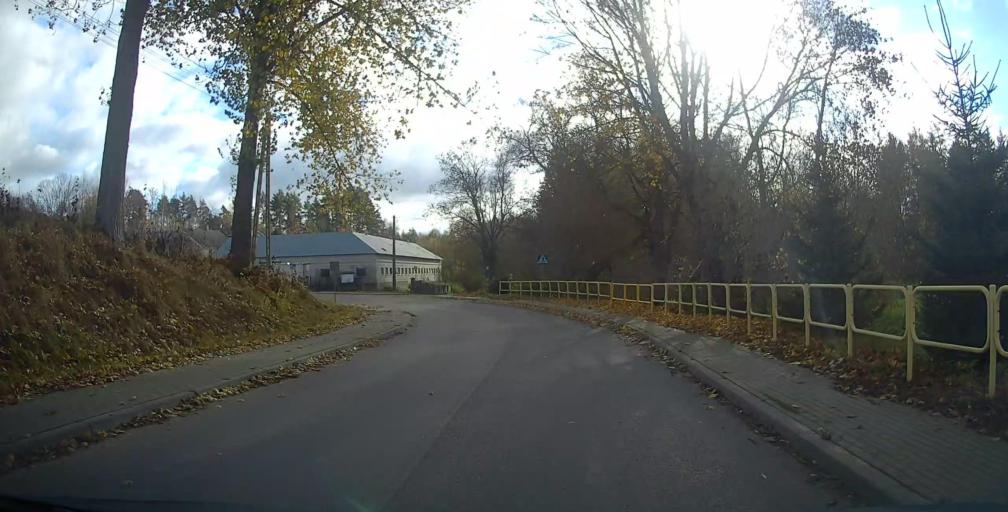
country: PL
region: Podlasie
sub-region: Suwalki
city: Suwalki
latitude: 54.2876
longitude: 22.8807
